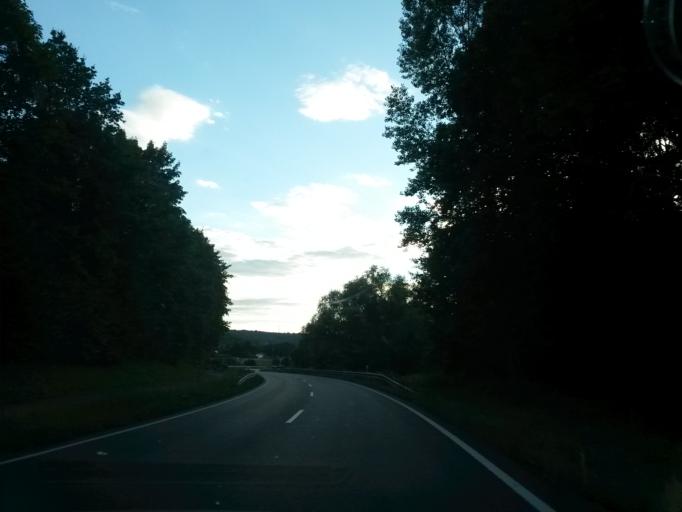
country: DE
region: Baden-Wuerttemberg
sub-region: Karlsruhe Region
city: Neuenburg
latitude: 48.8994
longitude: 8.5856
